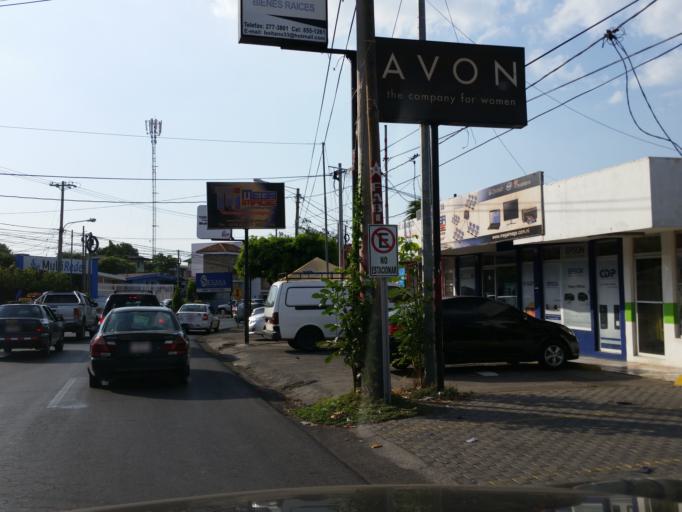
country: NI
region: Managua
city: Managua
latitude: 12.1182
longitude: -86.2523
